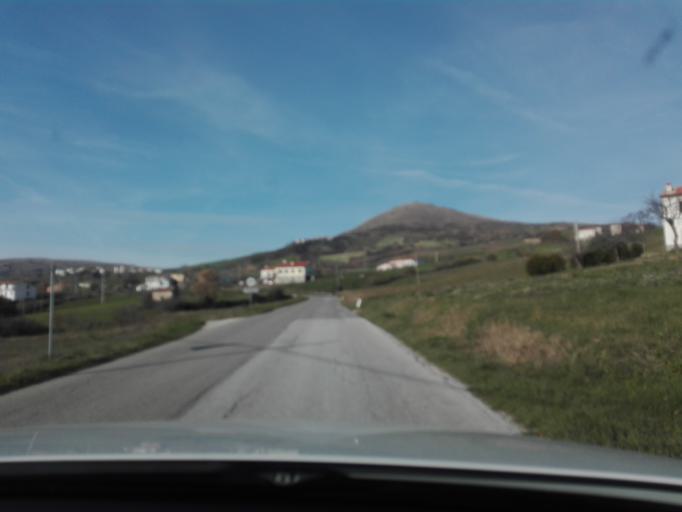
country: IT
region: Molise
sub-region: Provincia di Isernia
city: Agnone
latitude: 41.8349
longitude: 14.3829
